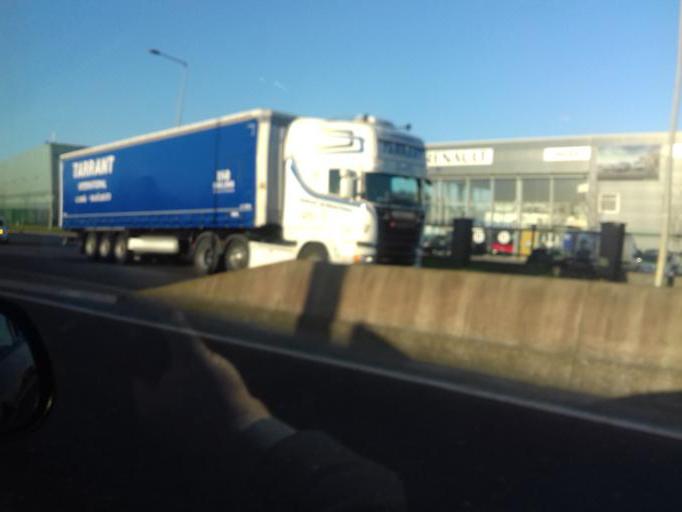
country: IE
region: Leinster
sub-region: Fingal County
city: Swords
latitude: 53.4924
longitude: -6.1960
